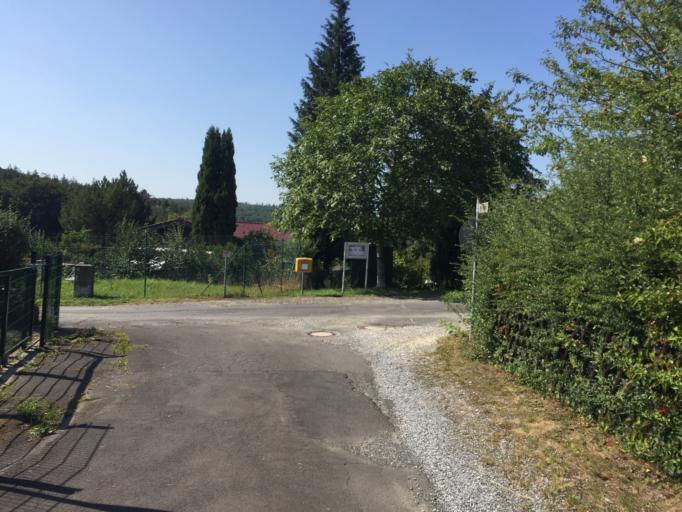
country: DE
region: Hesse
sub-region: Regierungsbezirk Darmstadt
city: Butzbach
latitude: 50.4201
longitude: 8.5892
